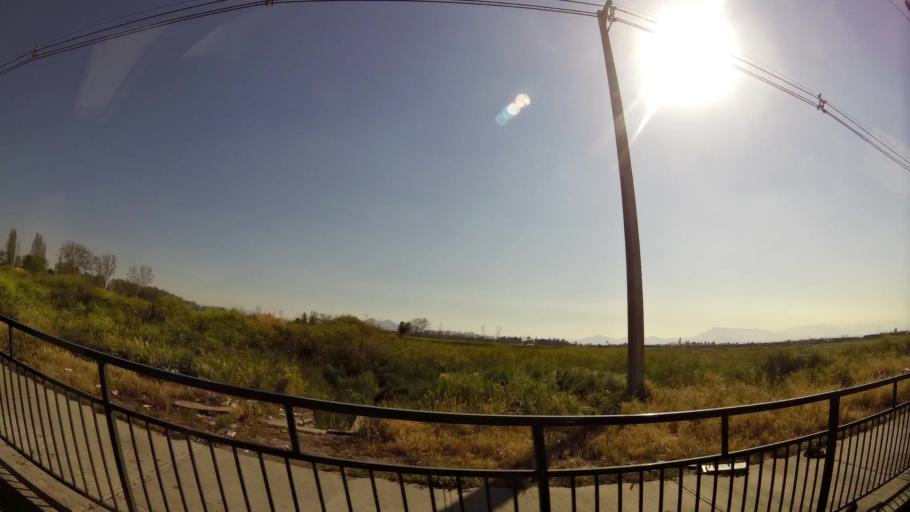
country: CL
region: Santiago Metropolitan
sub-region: Provincia de Santiago
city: La Pintana
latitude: -33.5686
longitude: -70.6134
